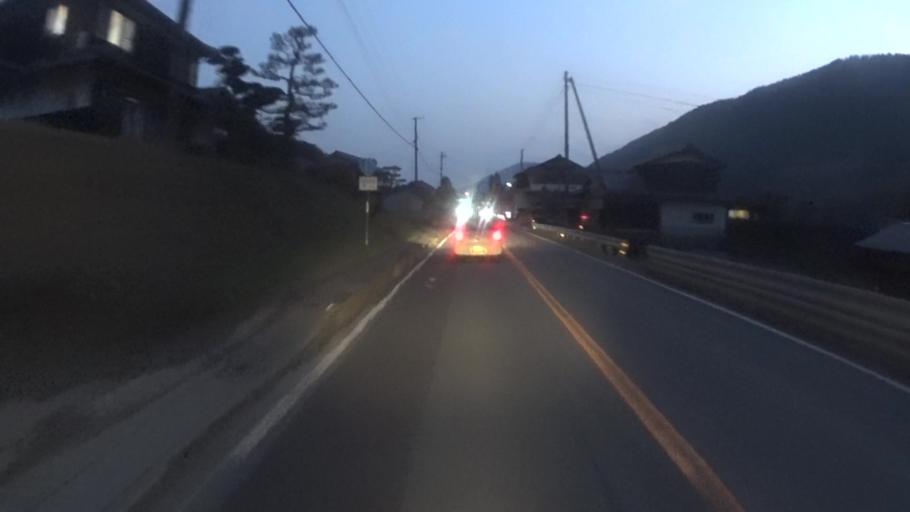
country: JP
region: Kyoto
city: Ayabe
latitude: 35.2346
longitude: 135.4131
